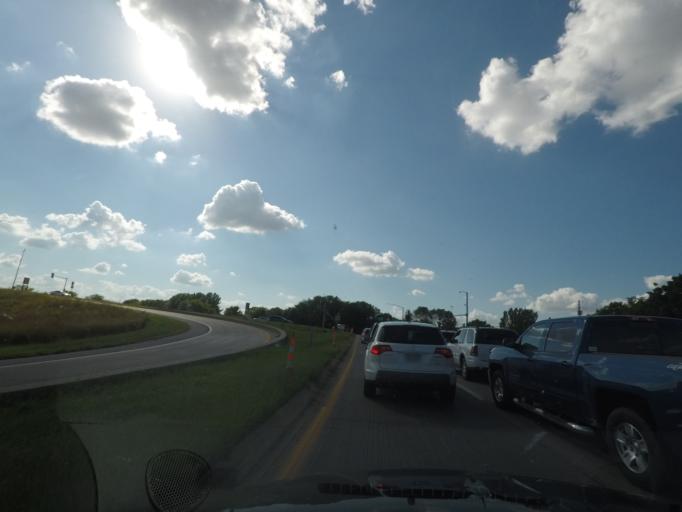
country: US
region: Iowa
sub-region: Dallas County
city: Waukee
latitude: 41.5932
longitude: -93.8080
